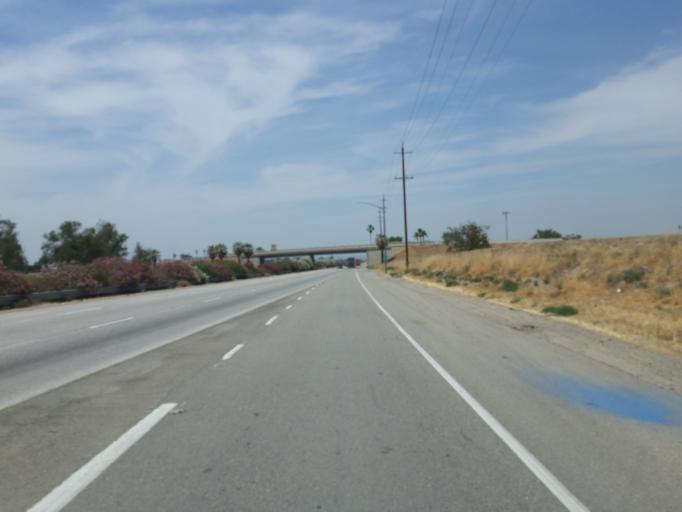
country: US
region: California
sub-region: Kern County
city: Weedpatch
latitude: 35.0554
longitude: -118.9669
